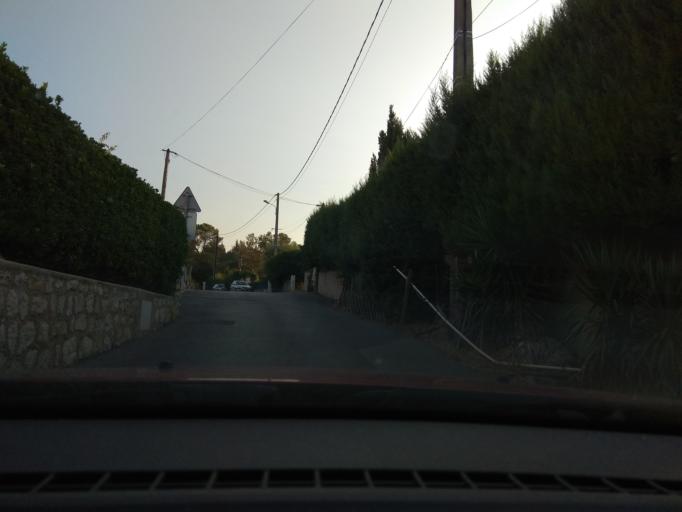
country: FR
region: Provence-Alpes-Cote d'Azur
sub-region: Departement des Alpes-Maritimes
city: Villeneuve-Loubet
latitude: 43.6764
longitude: 7.1118
